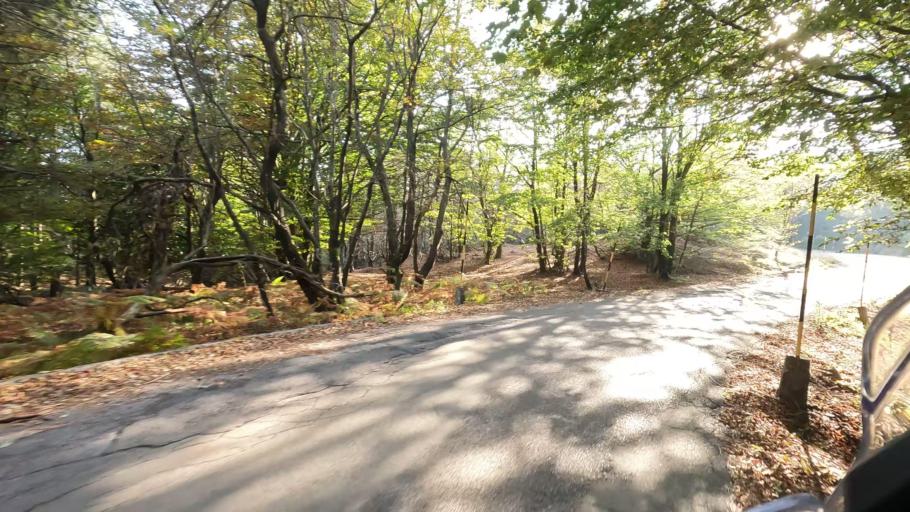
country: IT
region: Liguria
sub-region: Provincia di Savona
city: San Giovanni
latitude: 44.4305
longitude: 8.5440
